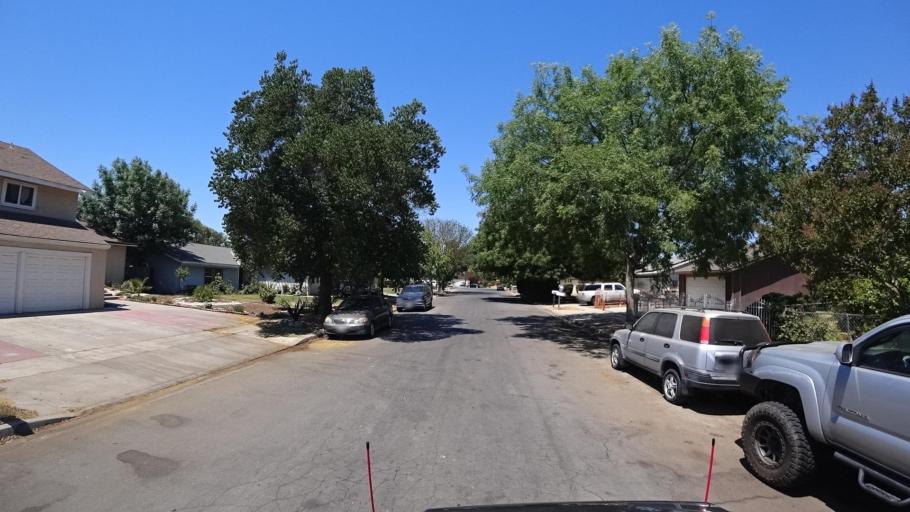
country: US
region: California
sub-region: Fresno County
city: Sunnyside
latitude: 36.7210
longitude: -119.7331
